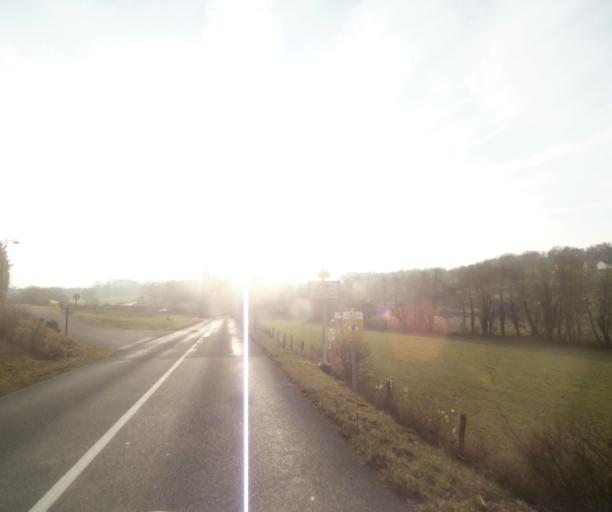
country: FR
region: Champagne-Ardenne
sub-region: Departement de la Marne
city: Sermaize-les-Bains
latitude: 48.7243
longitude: 4.9394
